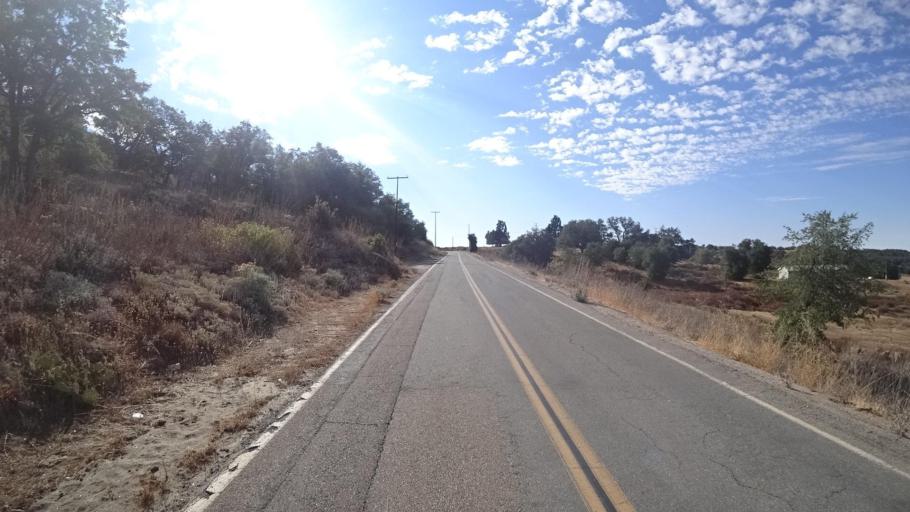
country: US
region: California
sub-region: San Diego County
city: Ramona
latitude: 33.1838
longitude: -116.7757
